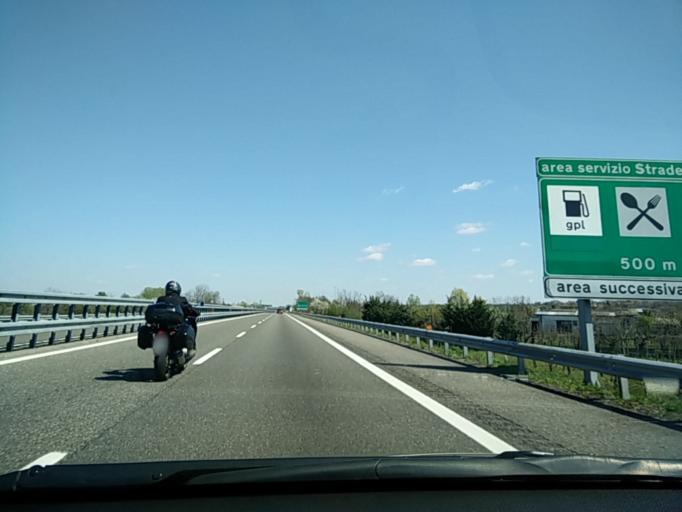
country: IT
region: Lombardy
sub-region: Provincia di Pavia
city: Stradella
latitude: 45.0831
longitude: 9.3077
